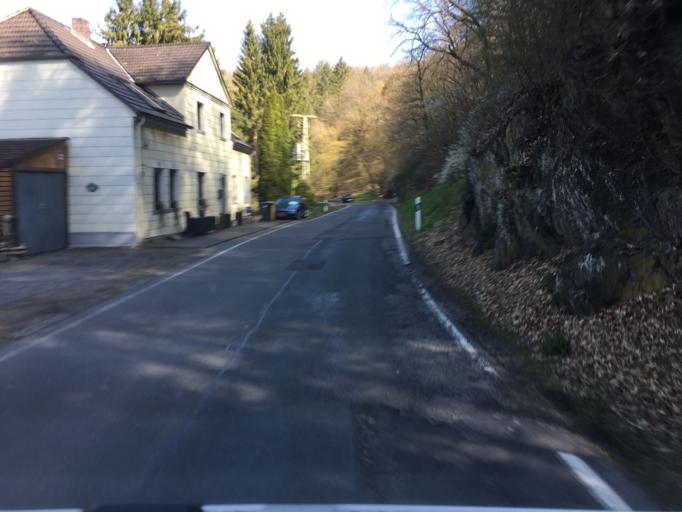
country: DE
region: Rheinland-Pfalz
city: Altenahr
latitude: 50.5119
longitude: 6.9687
